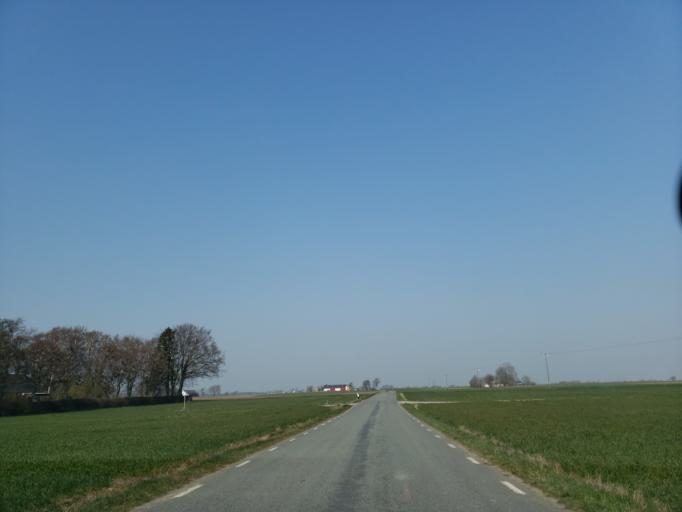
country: SE
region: Skane
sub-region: Simrishamns Kommun
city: Simrishamn
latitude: 55.4522
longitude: 14.2154
